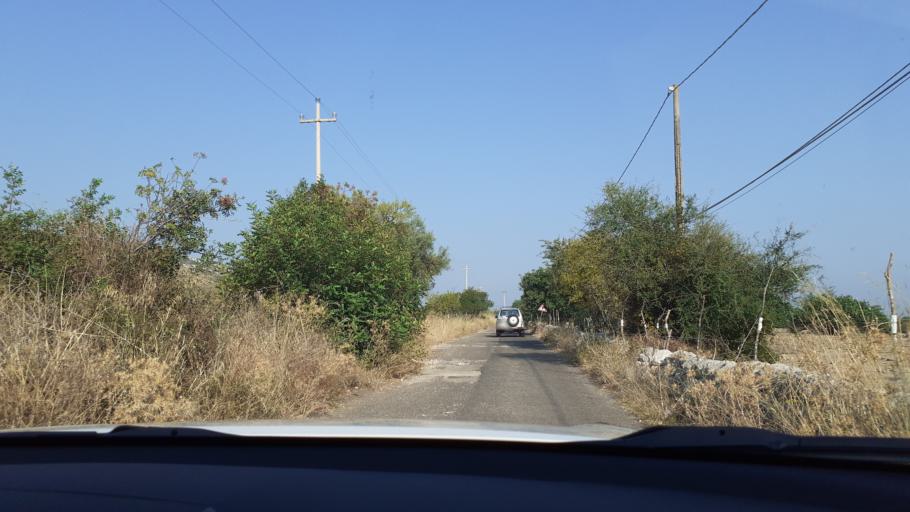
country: IT
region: Sicily
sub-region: Provincia di Siracusa
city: Cassibile
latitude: 36.9814
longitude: 15.1663
